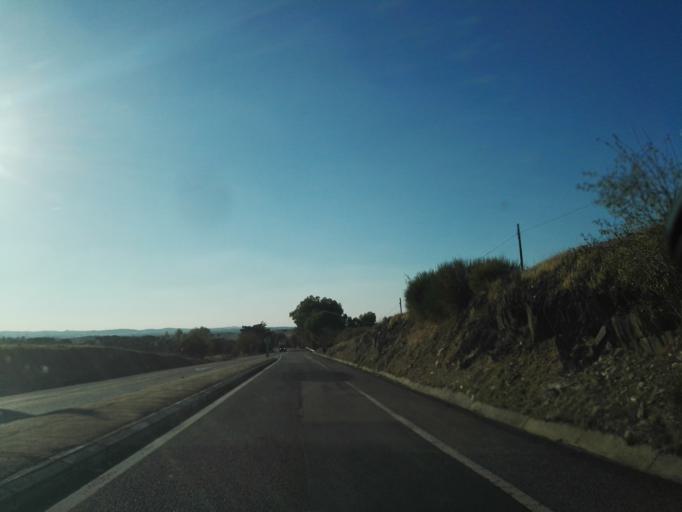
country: PT
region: Evora
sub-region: Vila Vicosa
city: Vila Vicosa
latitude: 38.8489
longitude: -7.3473
